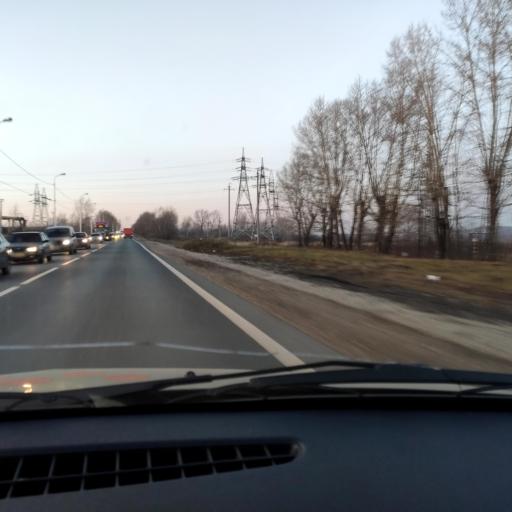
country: RU
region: Bashkortostan
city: Ufa
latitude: 54.8493
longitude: 56.1182
